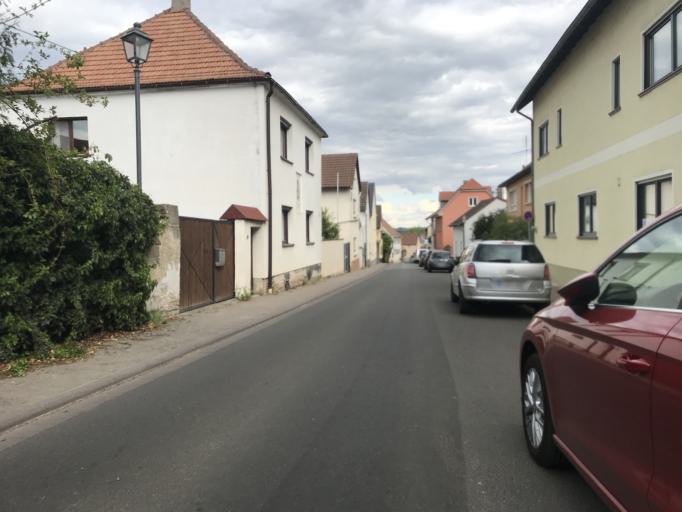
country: DE
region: Rheinland-Pfalz
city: Mommenheim
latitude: 49.8829
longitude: 8.2695
